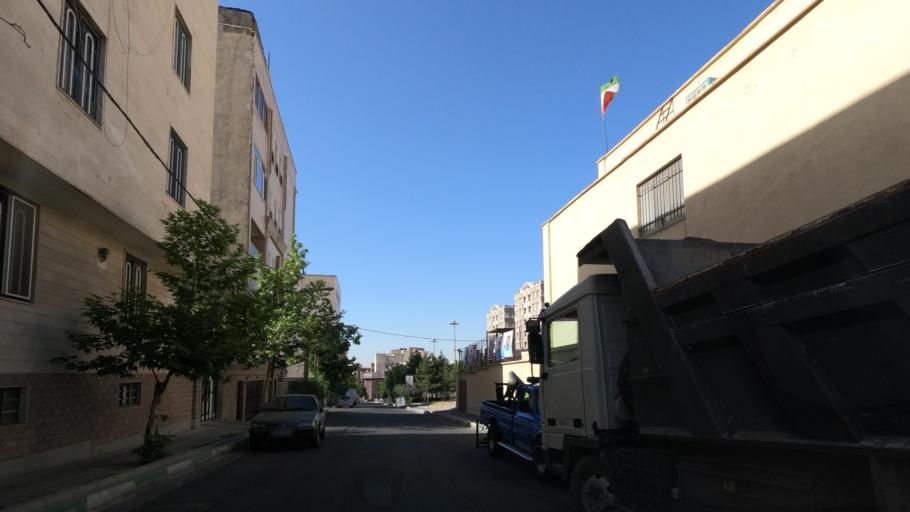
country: IR
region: Tehran
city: Tajrish
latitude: 35.7613
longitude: 51.3144
